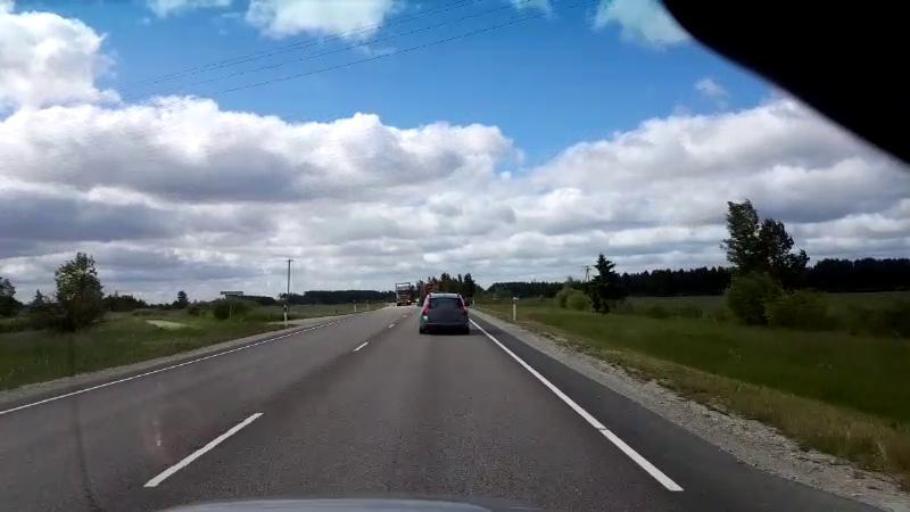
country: EE
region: Paernumaa
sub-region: Sauga vald
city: Sauga
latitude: 58.4879
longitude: 24.5286
